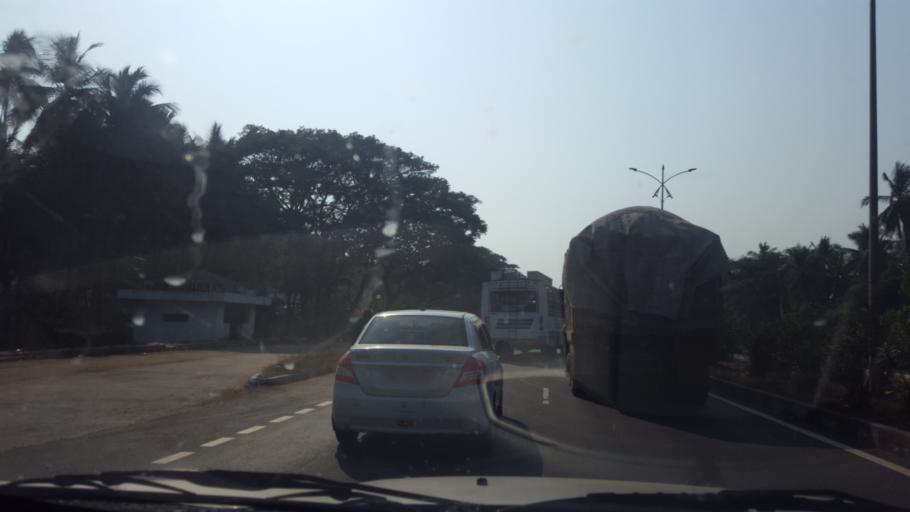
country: IN
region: Andhra Pradesh
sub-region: Vishakhapatnam
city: Anakapalle
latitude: 17.6753
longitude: 83.0088
